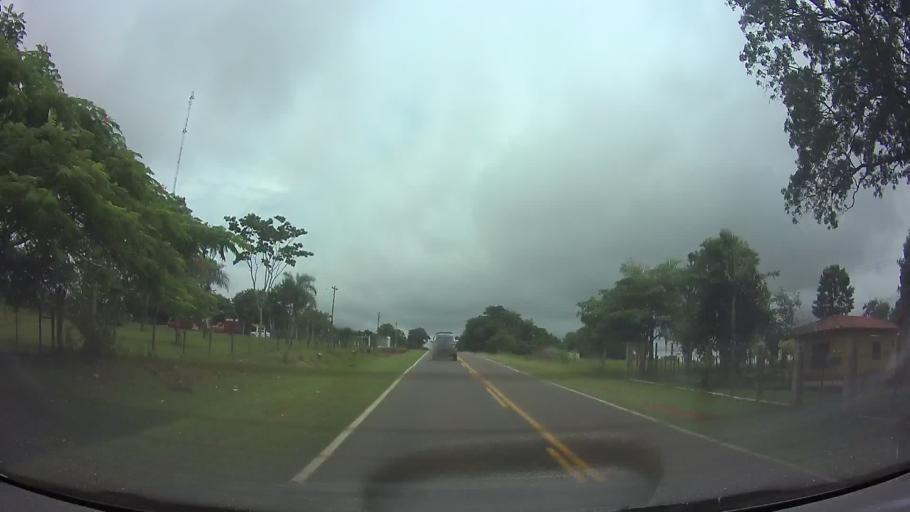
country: PY
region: Paraguari
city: Acahay
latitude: -25.9532
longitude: -57.0923
